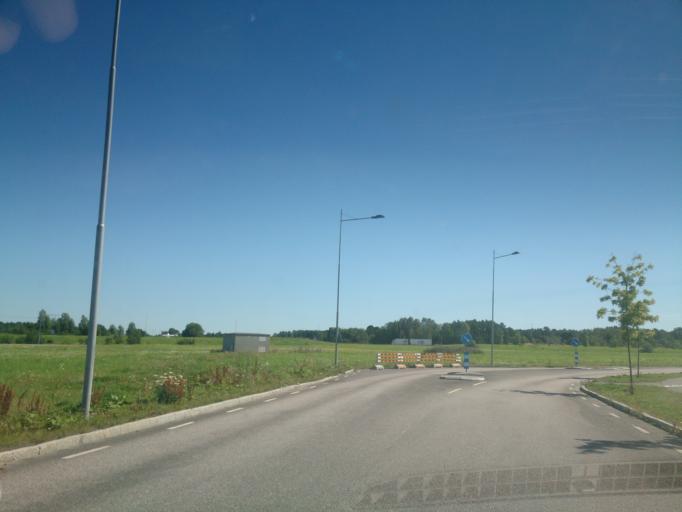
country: SE
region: OEstergoetland
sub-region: Linkopings Kommun
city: Linkoping
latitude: 58.4306
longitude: 15.6631
